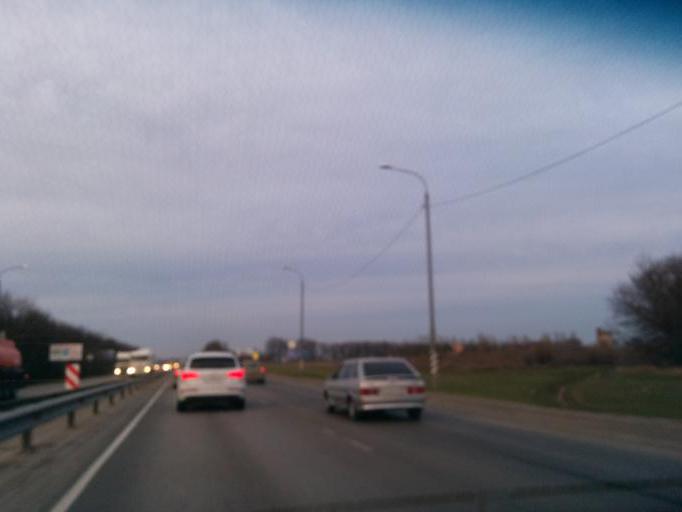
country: RU
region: Rostov
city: Grushevskaya
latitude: 47.3656
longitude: 39.8947
